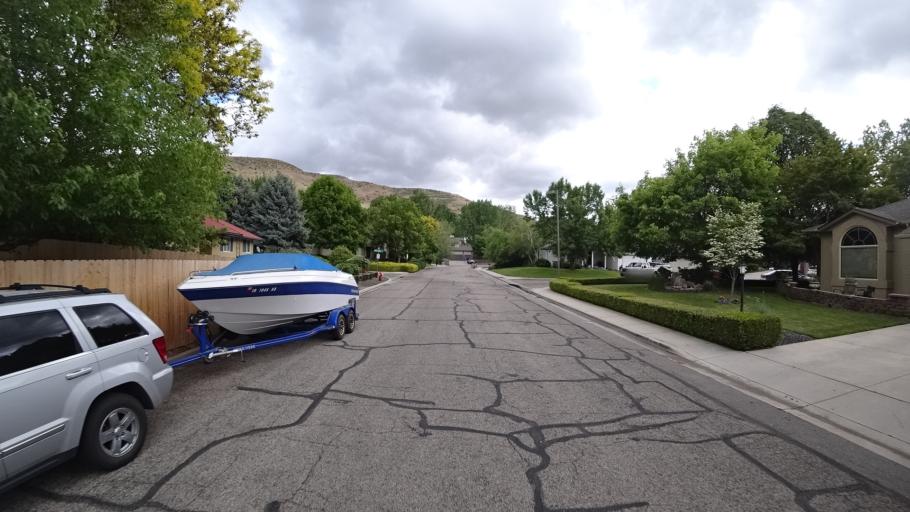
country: US
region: Idaho
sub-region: Ada County
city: Garden City
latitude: 43.6708
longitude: -116.2583
